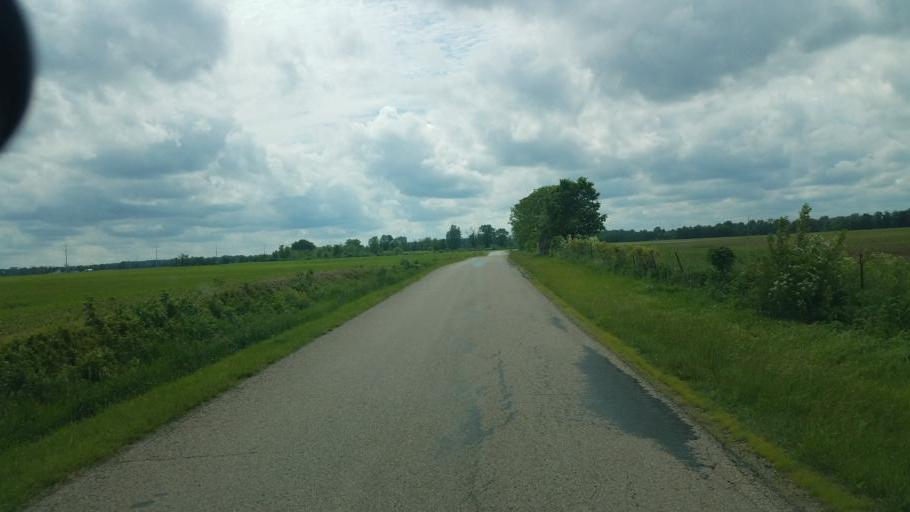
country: US
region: Ohio
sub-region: Fairfield County
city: Millersport
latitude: 39.9371
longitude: -82.5685
